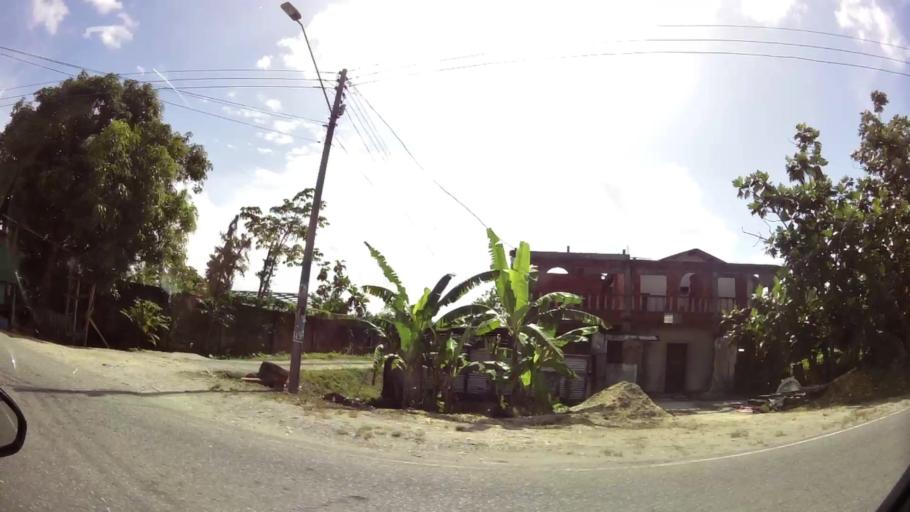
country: TT
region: Borough of Arima
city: Arima
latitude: 10.6212
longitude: -61.2550
